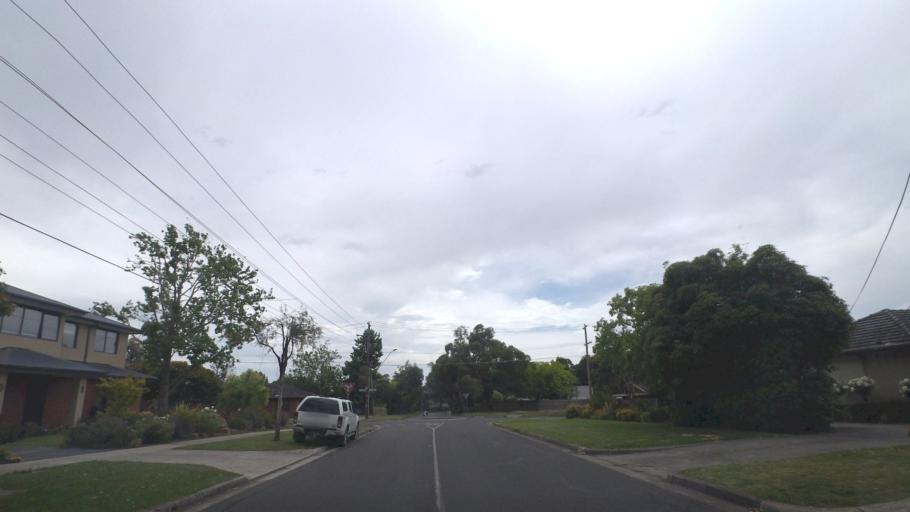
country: AU
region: Victoria
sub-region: Maroondah
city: Croydon North
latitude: -37.7960
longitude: 145.3012
